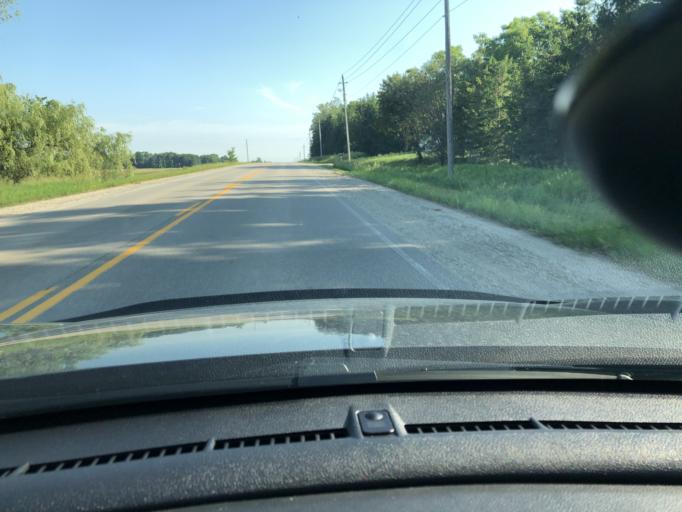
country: CA
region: Ontario
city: Stratford
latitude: 43.3985
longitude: -80.8375
